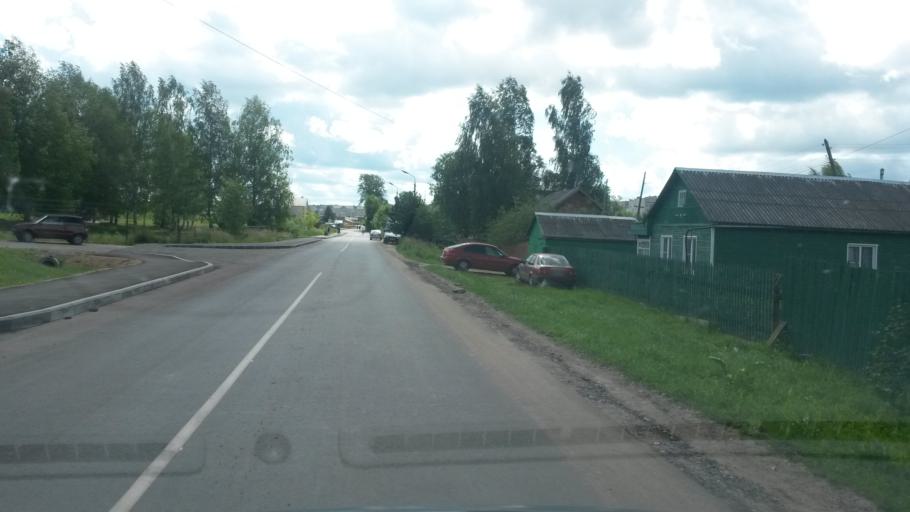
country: RU
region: Jaroslavl
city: Gavrilov-Yam
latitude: 57.3109
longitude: 39.8653
